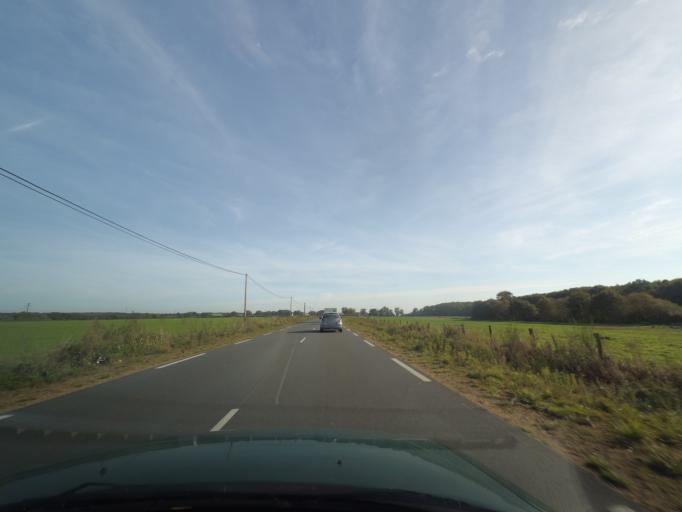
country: FR
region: Pays de la Loire
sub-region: Departement de la Vendee
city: Tiffauges
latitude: 47.0269
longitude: -1.0996
